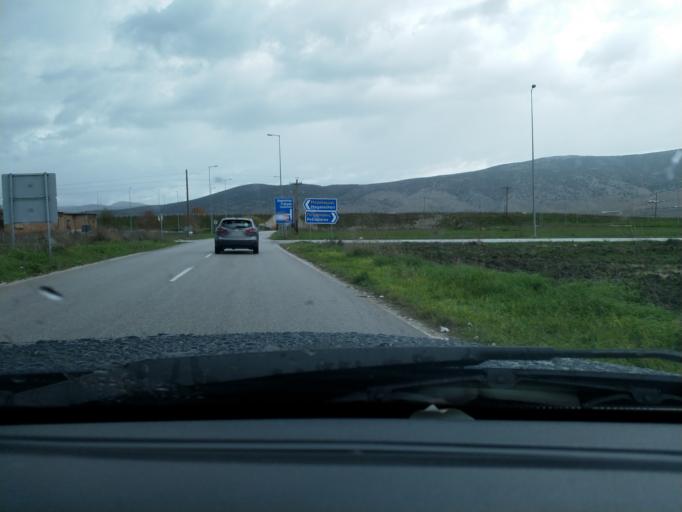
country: GR
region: Thessaly
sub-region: Trikala
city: Taxiarches
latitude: 39.5598
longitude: 21.8896
